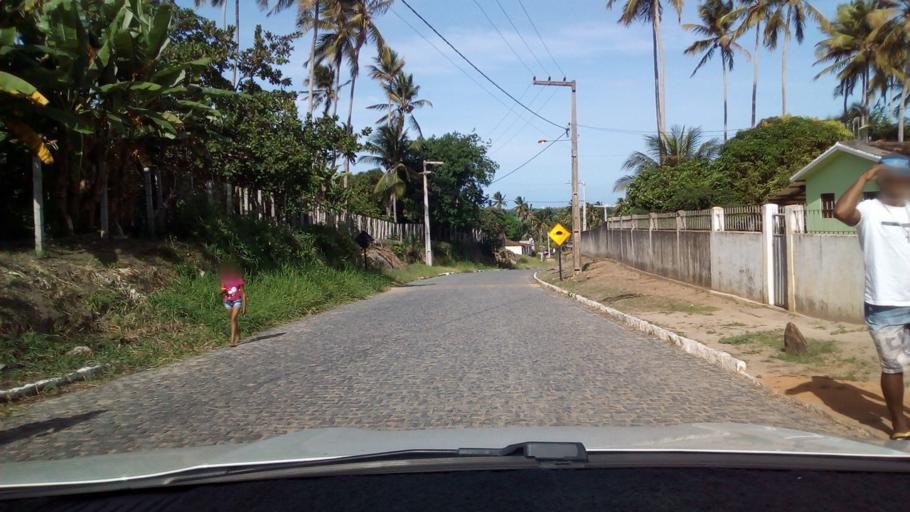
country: BR
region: Paraiba
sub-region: Joao Pessoa
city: Joao Pessoa
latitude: -7.0514
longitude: -34.9010
